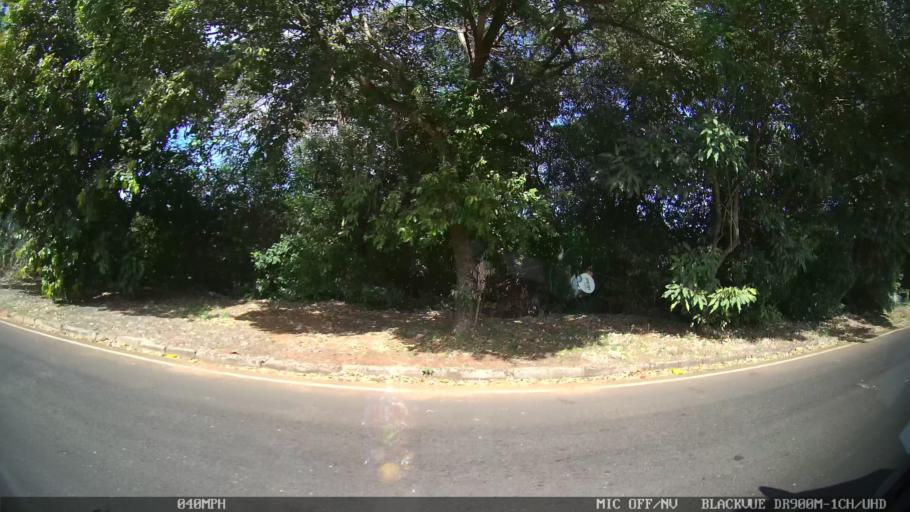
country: BR
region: Sao Paulo
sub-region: Sao Jose Do Rio Preto
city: Sao Jose do Rio Preto
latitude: -20.8470
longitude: -49.3610
